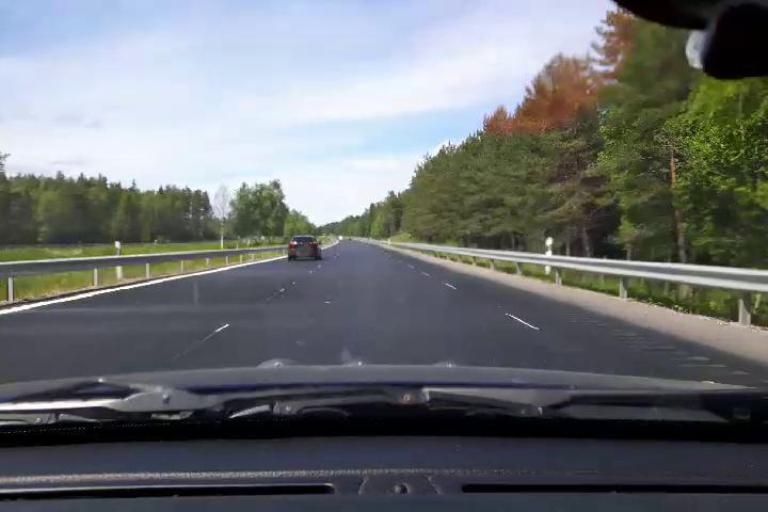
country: SE
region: Gaevleborg
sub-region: Gavle Kommun
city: Gavle
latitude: 60.5982
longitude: 17.1861
